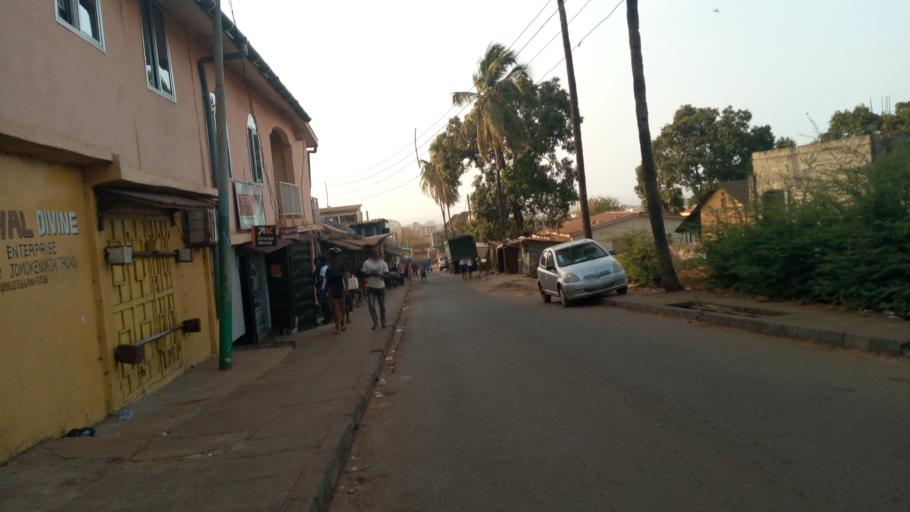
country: SL
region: Western Area
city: Freetown
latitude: 8.4707
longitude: -13.2426
